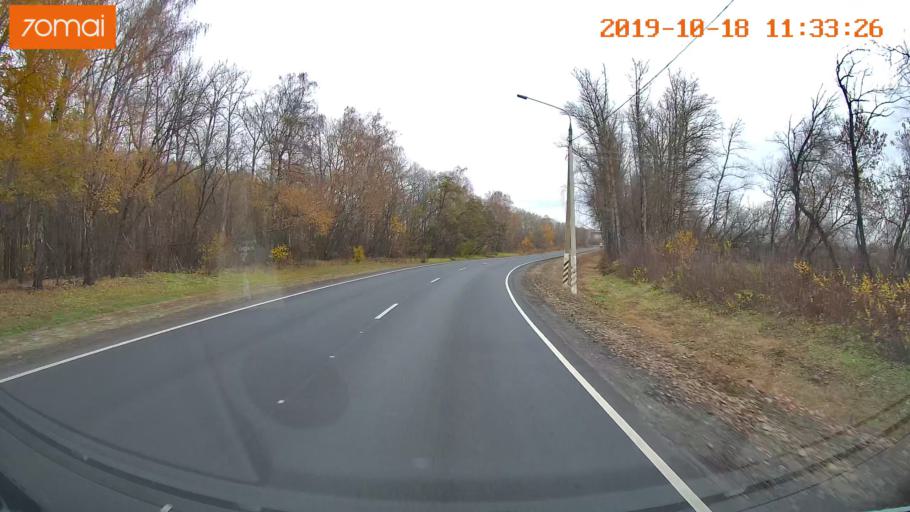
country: RU
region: Rjazan
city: Oktyabr'skiy
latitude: 54.1412
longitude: 38.7402
